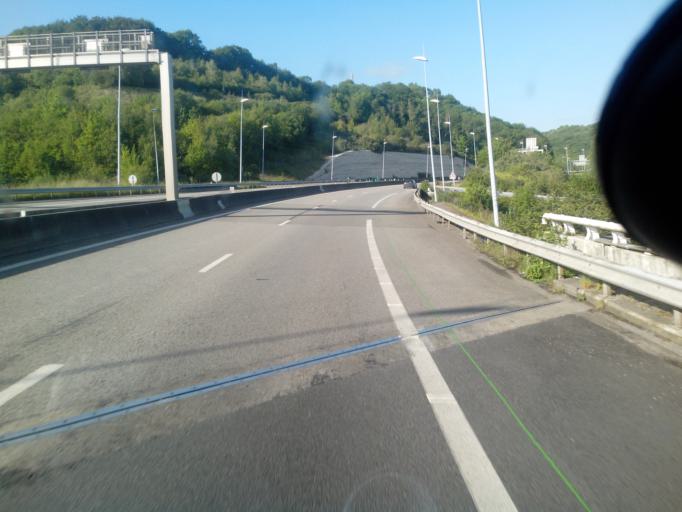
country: FR
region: Haute-Normandie
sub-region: Departement de la Seine-Maritime
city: Rogerville
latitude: 49.4971
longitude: 0.2679
